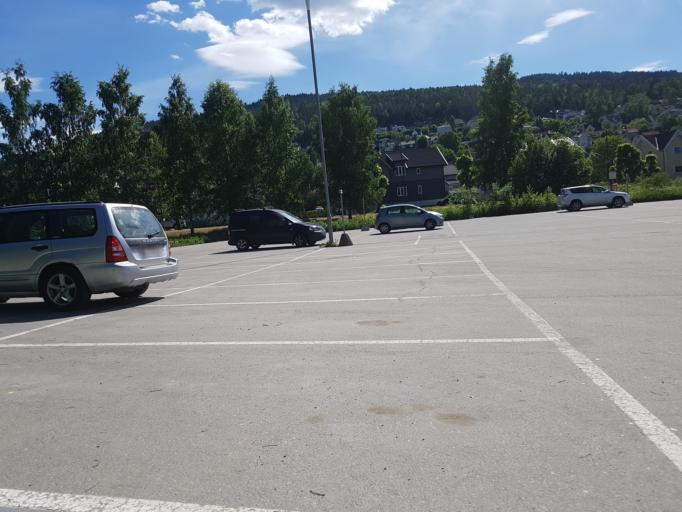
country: NO
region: Buskerud
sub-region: Drammen
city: Drammen
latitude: 59.7392
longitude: 10.1820
